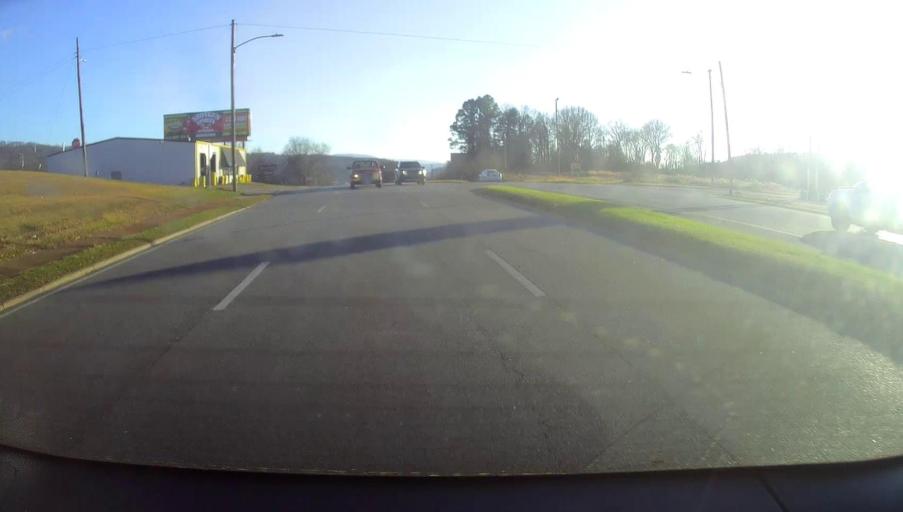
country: US
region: Alabama
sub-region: Calhoun County
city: Anniston
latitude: 33.6497
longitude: -85.8266
